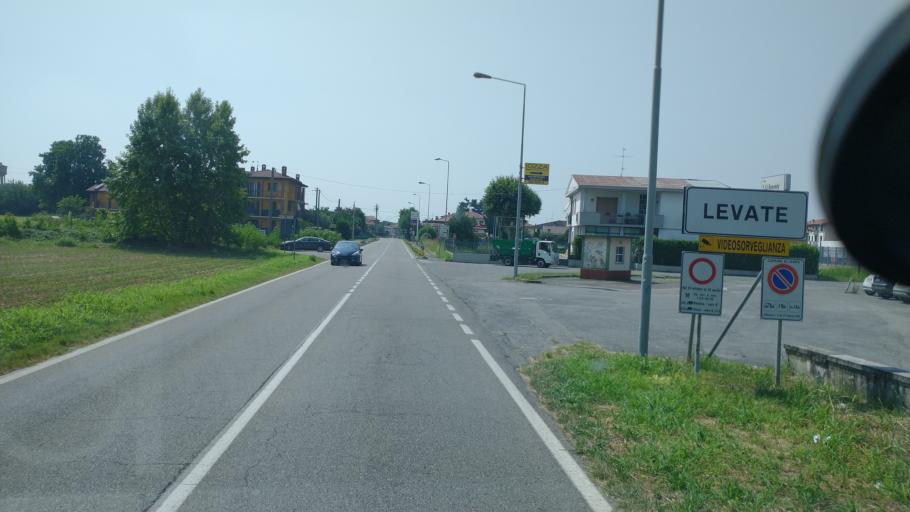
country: IT
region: Lombardy
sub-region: Provincia di Bergamo
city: Levate
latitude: 45.6297
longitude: 9.6199
